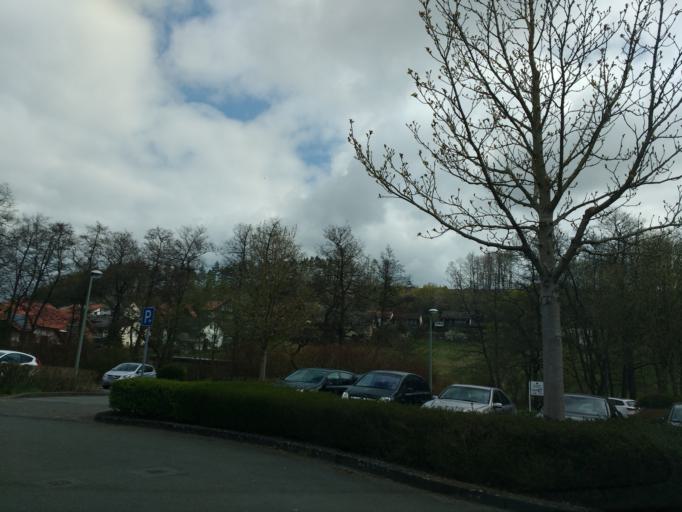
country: DE
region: North Rhine-Westphalia
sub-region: Regierungsbezirk Detmold
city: Wunnenberg
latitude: 51.5182
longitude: 8.7023
